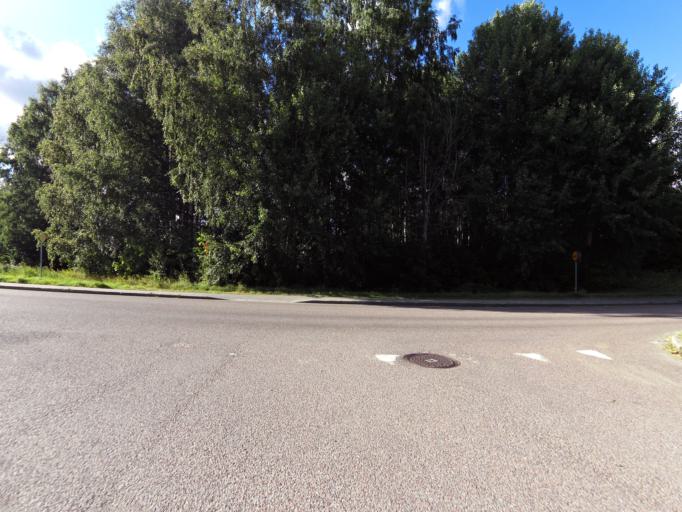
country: SE
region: Gaevleborg
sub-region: Gavle Kommun
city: Gavle
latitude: 60.6951
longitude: 17.1603
